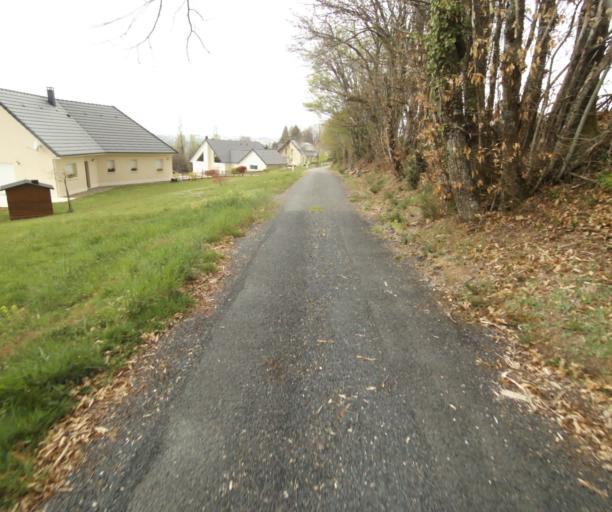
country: FR
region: Limousin
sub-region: Departement de la Correze
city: Naves
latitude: 45.3047
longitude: 1.8127
